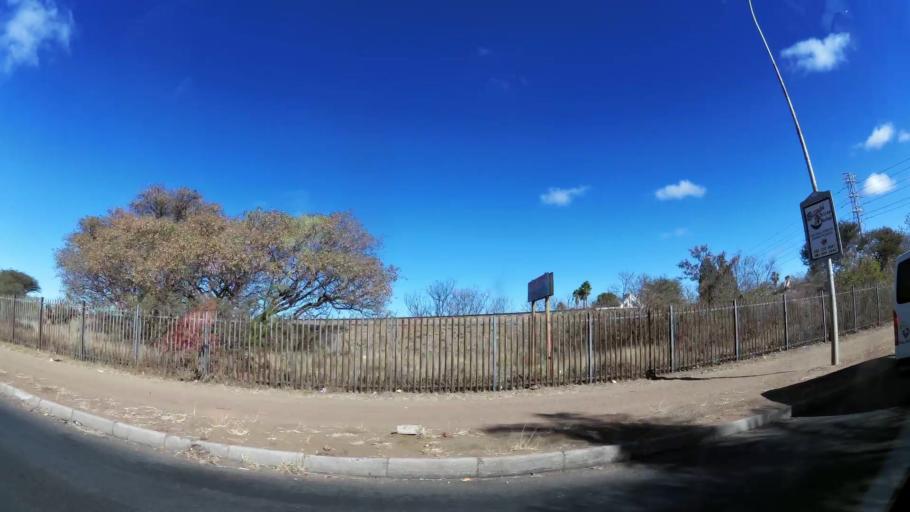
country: ZA
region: Limpopo
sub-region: Capricorn District Municipality
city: Polokwane
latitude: -23.8829
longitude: 29.4430
